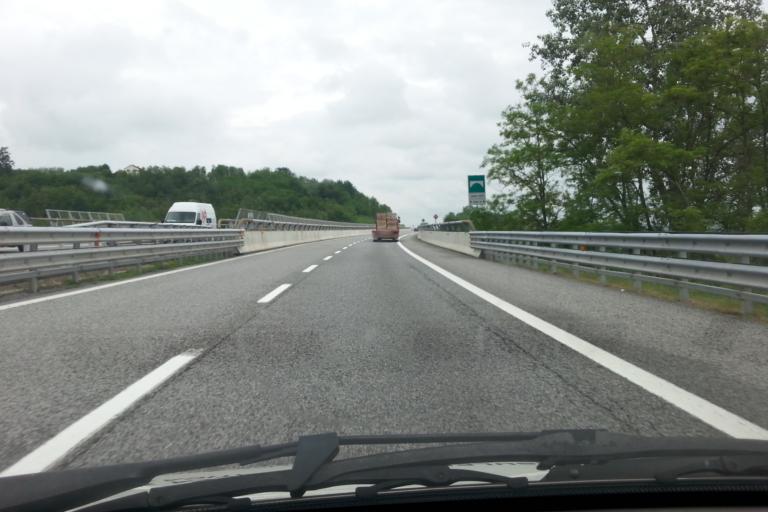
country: IT
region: Piedmont
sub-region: Provincia di Cuneo
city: Bastia Mondovi
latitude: 44.4181
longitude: 7.8928
